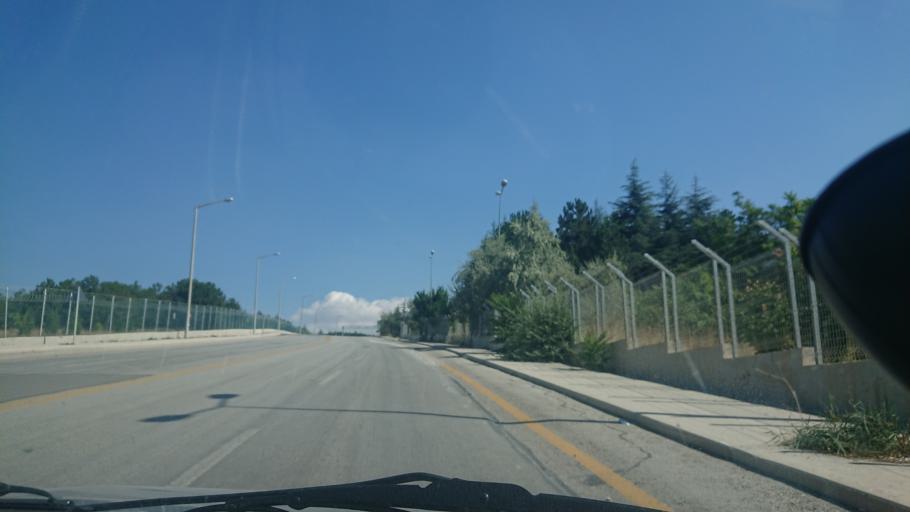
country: TR
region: Ankara
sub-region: Goelbasi
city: Golbasi
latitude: 39.8069
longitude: 32.8256
